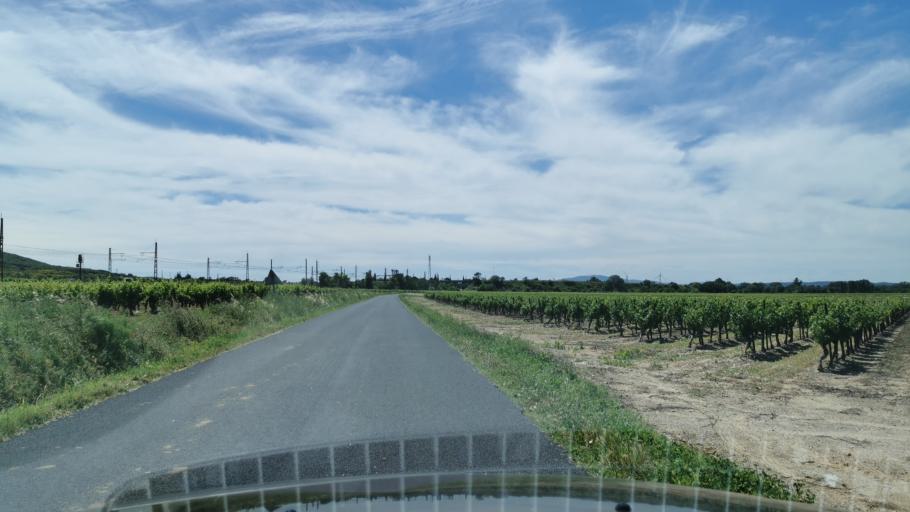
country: FR
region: Languedoc-Roussillon
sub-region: Departement de l'Aude
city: Nevian
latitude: 43.2133
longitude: 2.8812
